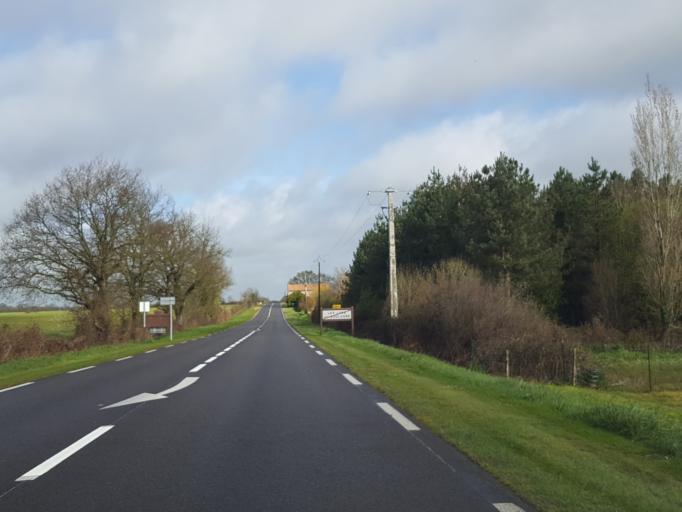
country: FR
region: Pays de la Loire
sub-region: Departement de la Vendee
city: Les Lucs-sur-Boulogne
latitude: 46.8509
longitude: -1.4953
